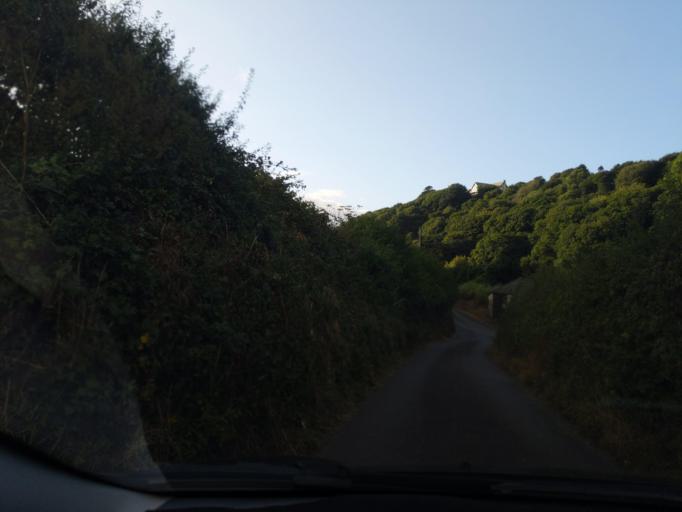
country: GB
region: England
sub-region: Devon
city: Salcombe
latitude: 50.2257
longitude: -3.7896
